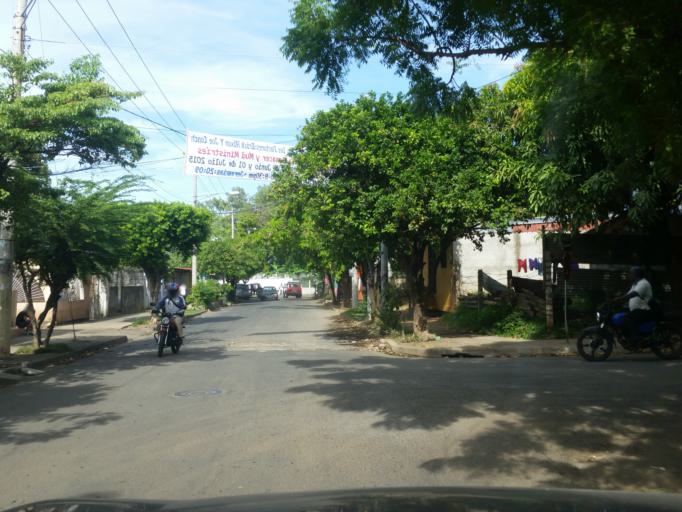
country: NI
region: Managua
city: Managua
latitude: 12.1236
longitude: -86.2474
